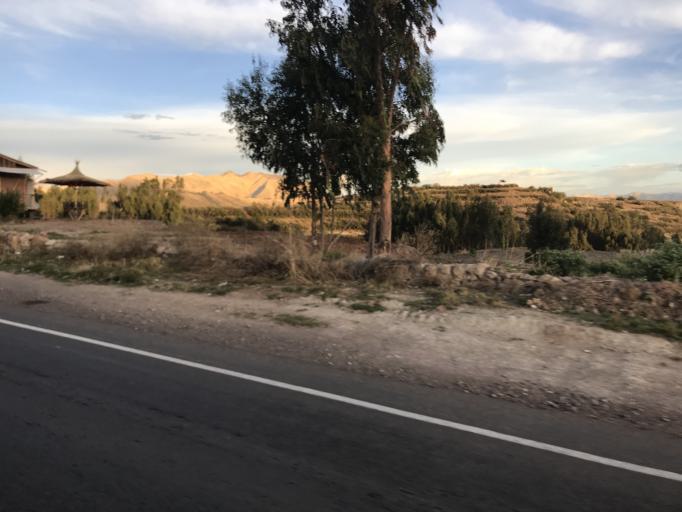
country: PE
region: Cusco
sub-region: Provincia de Cusco
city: Cusco
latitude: -13.4916
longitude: -71.9658
